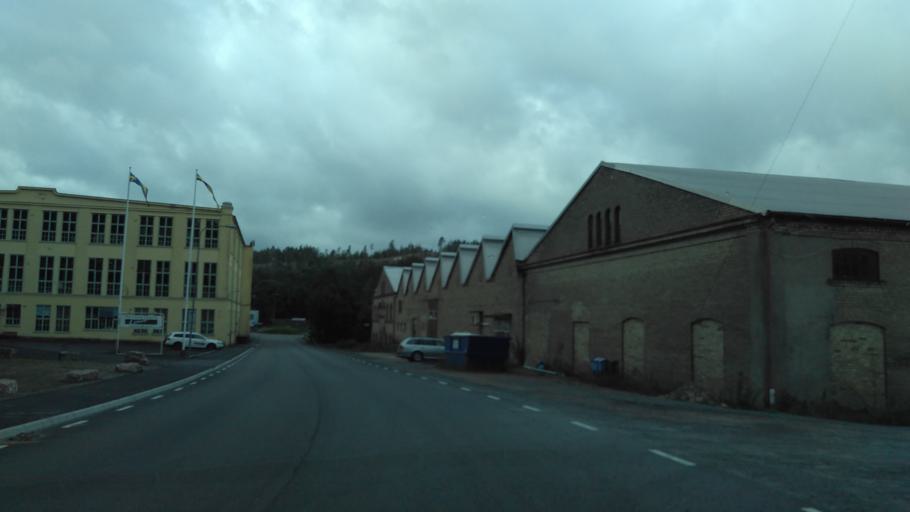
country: SE
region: Vaestra Goetaland
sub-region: Marks Kommun
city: Fritsla
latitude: 57.5642
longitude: 12.7863
